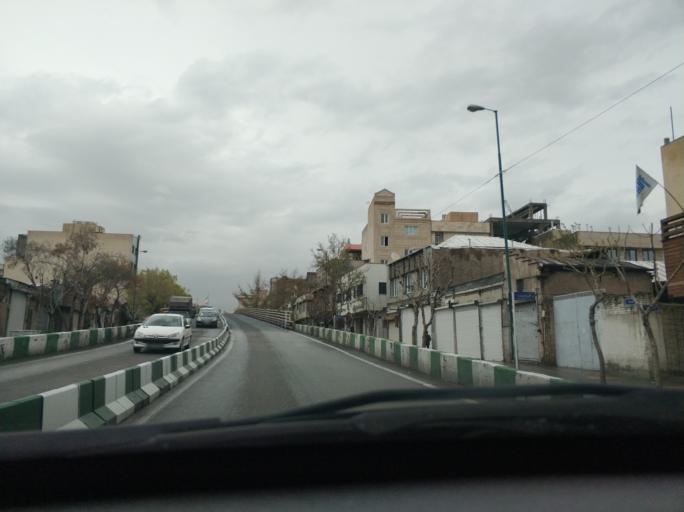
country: IR
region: Tehran
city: Tehran
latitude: 35.7005
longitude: 51.4380
